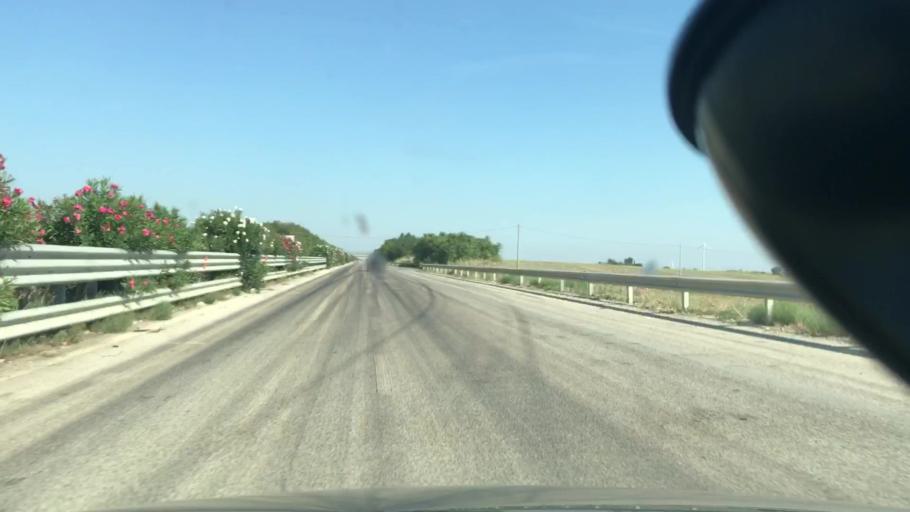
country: IT
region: Apulia
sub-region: Provincia di Foggia
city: Ascoli Satriano
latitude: 41.2808
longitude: 15.5540
